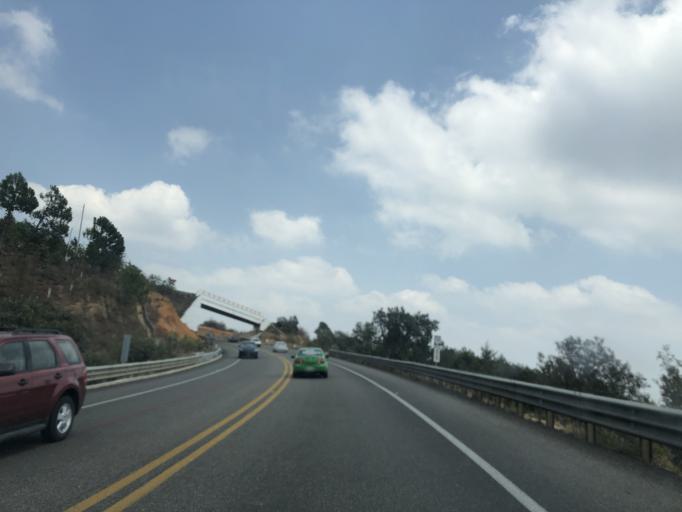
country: MX
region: Chiapas
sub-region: Zinacantan
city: Nachig
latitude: 16.6872
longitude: -92.7351
